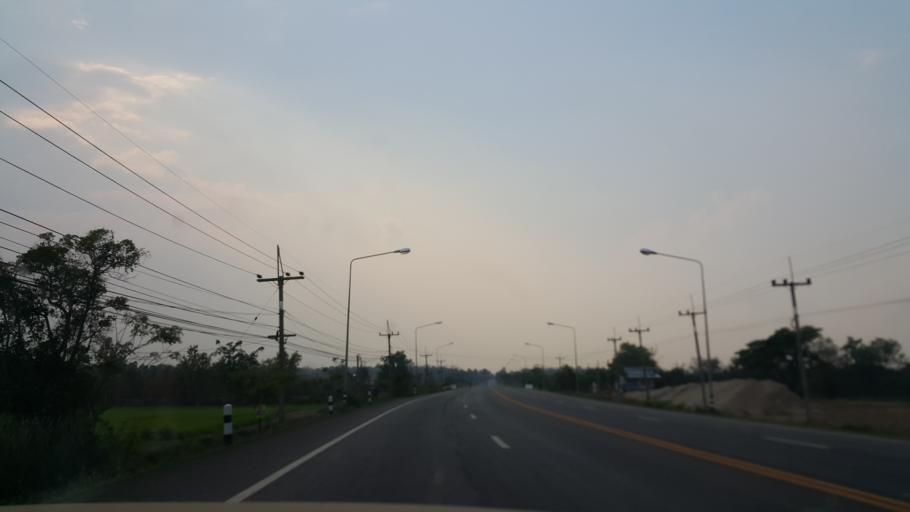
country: TH
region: Nakhon Phanom
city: Renu Nakhon
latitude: 17.0222
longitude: 104.7200
